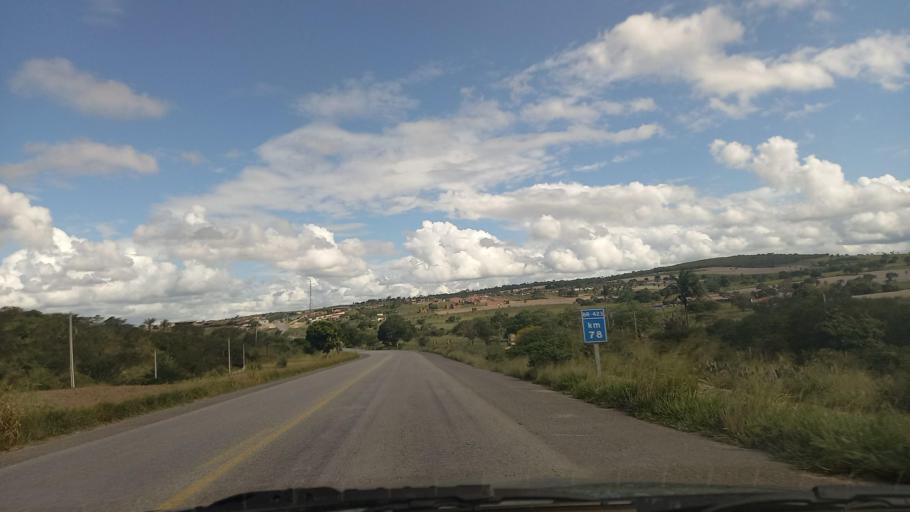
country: BR
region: Pernambuco
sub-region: Lajedo
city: Lajedo
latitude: -8.7445
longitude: -36.4313
